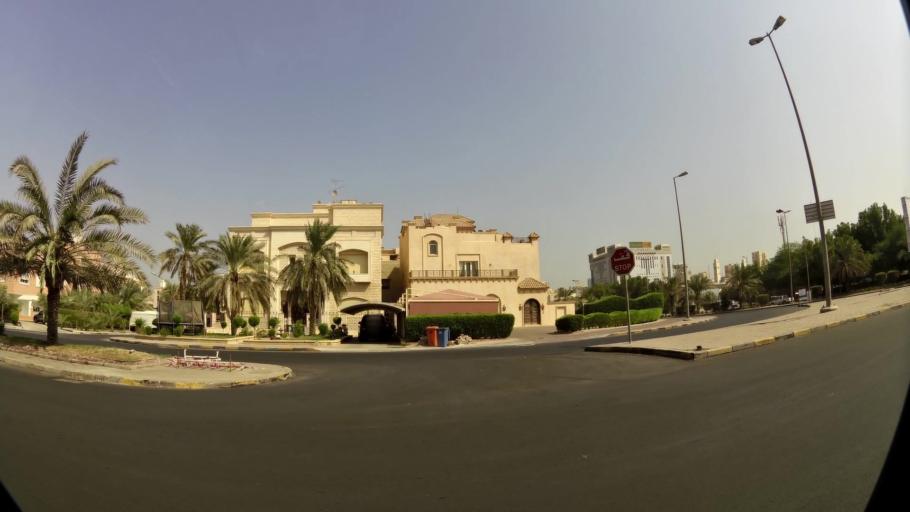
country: KW
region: Al Asimah
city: Ad Dasmah
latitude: 29.3432
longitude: 48.0043
